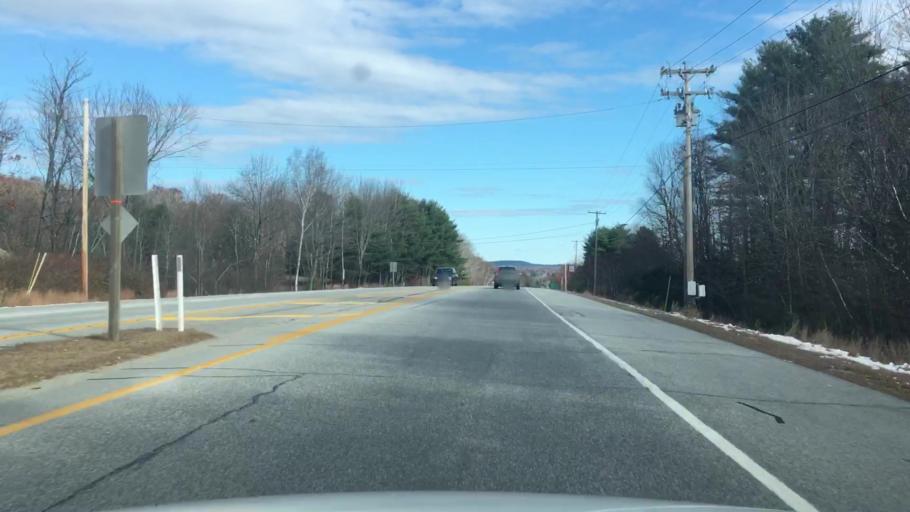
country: US
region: Maine
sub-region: Kennebec County
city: Winthrop
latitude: 44.3085
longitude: -69.9535
